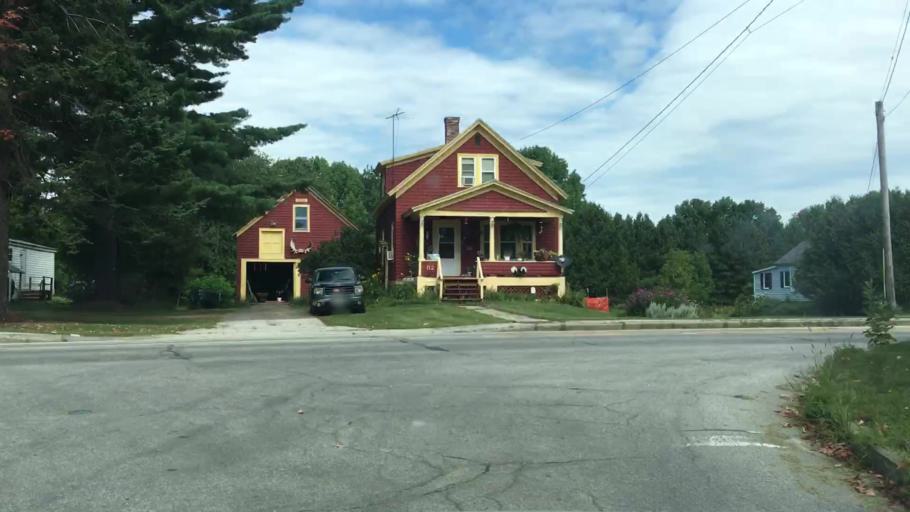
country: US
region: Maine
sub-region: Piscataquis County
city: Dover-Foxcroft
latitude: 45.1909
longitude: -69.2232
